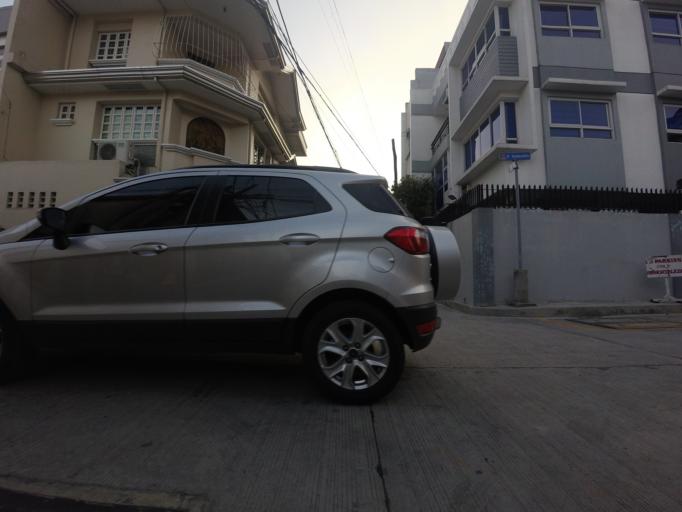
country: PH
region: Metro Manila
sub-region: San Juan
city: San Juan
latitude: 14.6001
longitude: 121.0318
